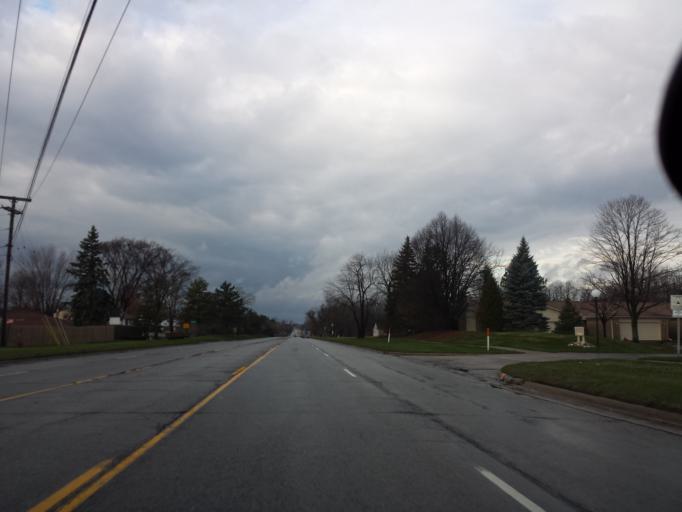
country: US
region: Michigan
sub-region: Oakland County
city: Bingham Farms
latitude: 42.5015
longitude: -83.2656
